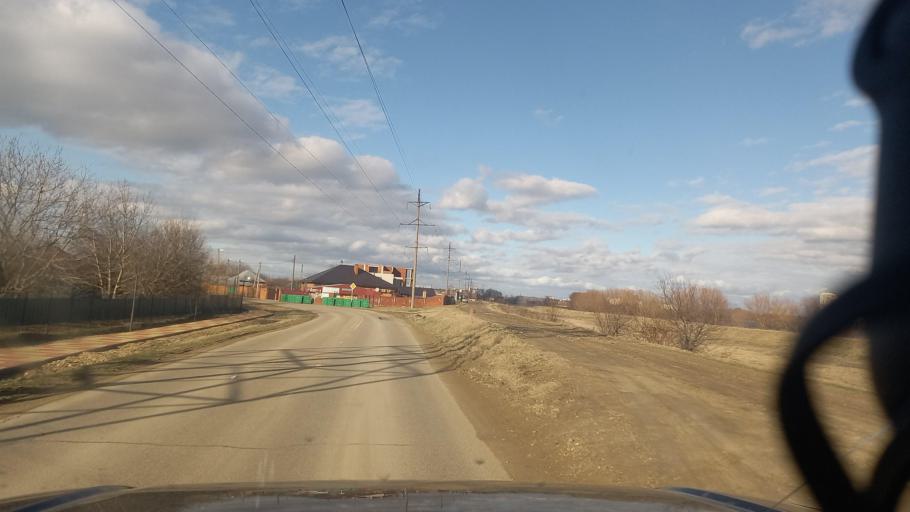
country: RU
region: Adygeya
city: Yablonovskiy
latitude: 45.0296
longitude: 38.8976
